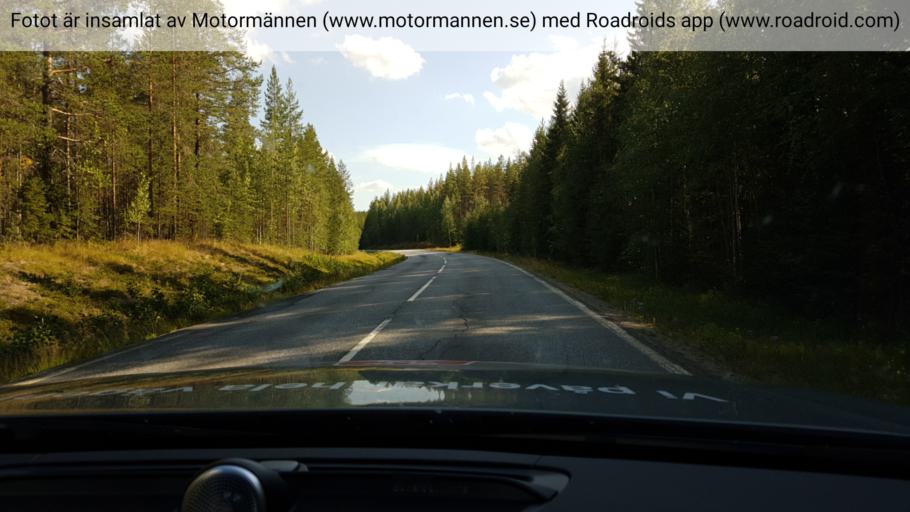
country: SE
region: Vaesterbotten
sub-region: Dorotea Kommun
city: Dorotea
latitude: 63.8845
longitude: 16.3709
